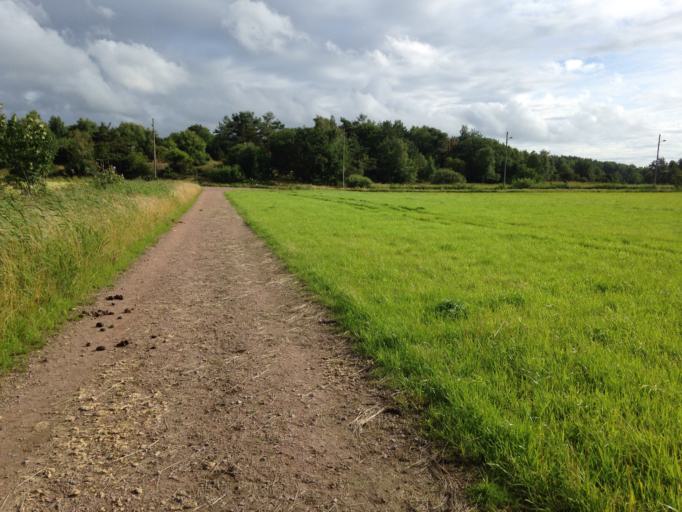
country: SE
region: Vaestra Goetaland
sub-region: Goteborg
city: Majorna
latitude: 57.8033
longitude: 11.8853
